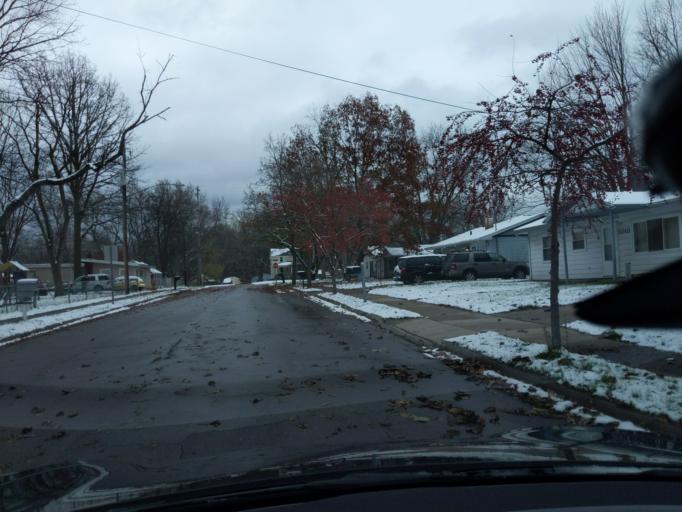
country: US
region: Michigan
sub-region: Ingham County
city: Lansing
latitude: 42.6839
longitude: -84.5886
